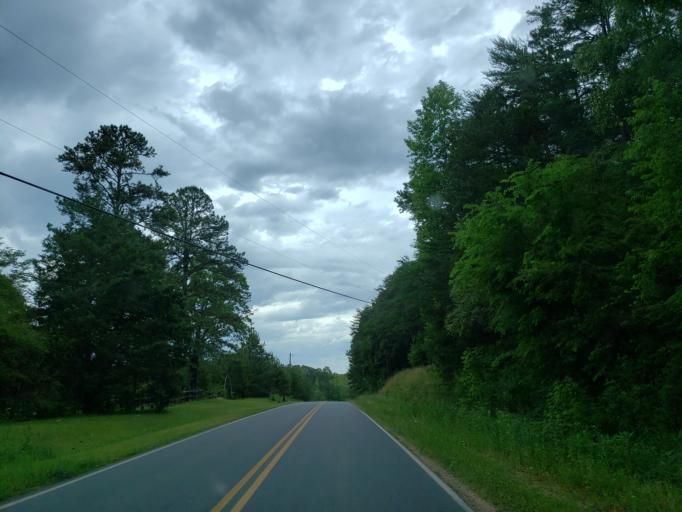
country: US
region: Georgia
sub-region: Polk County
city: Rockmart
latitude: 33.9710
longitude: -85.0461
